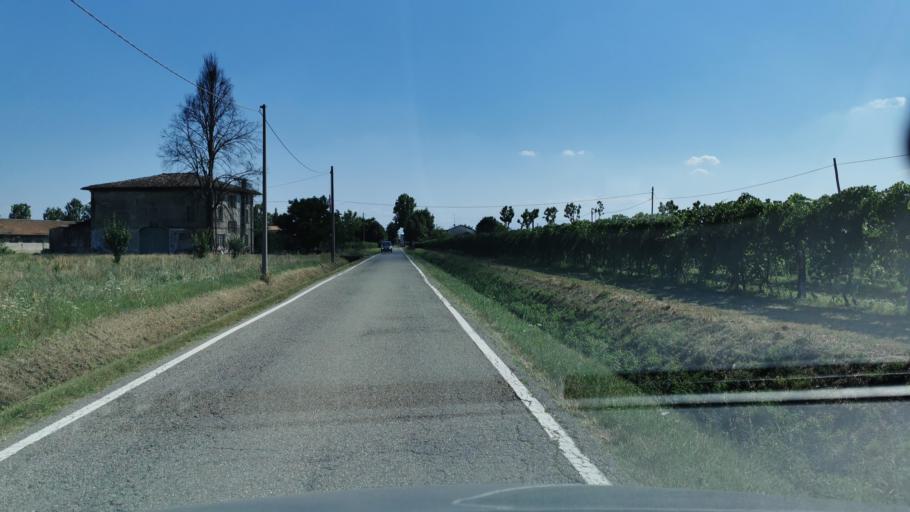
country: IT
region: Emilia-Romagna
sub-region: Provincia di Modena
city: Limidi
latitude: 44.7690
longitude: 10.9168
